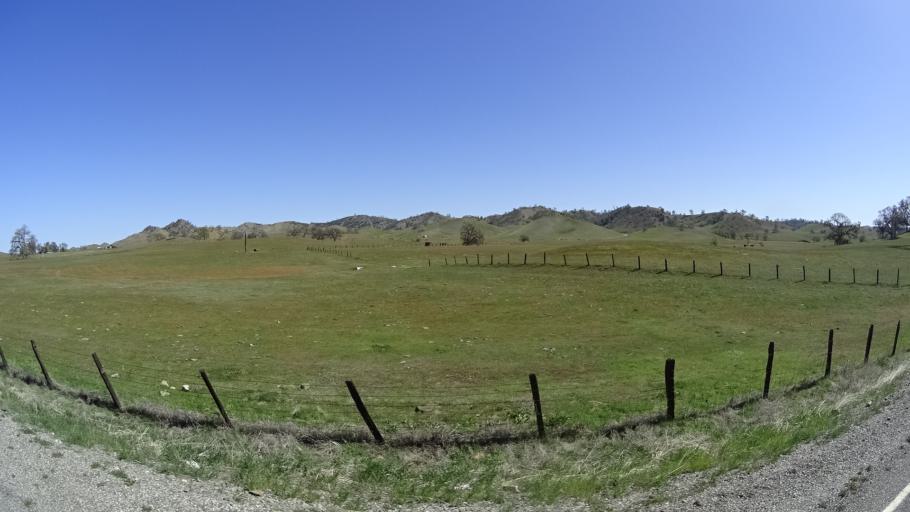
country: US
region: California
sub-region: Glenn County
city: Orland
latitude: 39.6872
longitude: -122.5433
